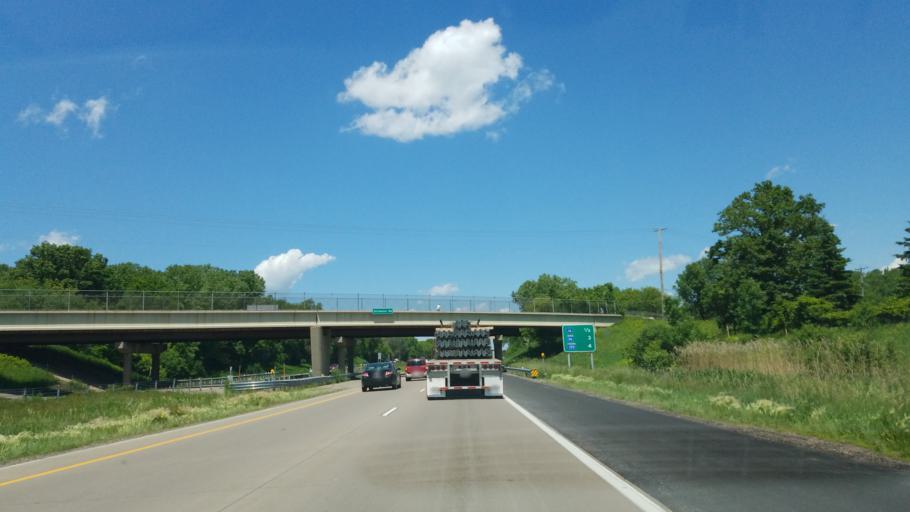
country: US
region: Minnesota
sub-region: Washington County
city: Oakdale
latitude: 44.9864
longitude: -92.9604
